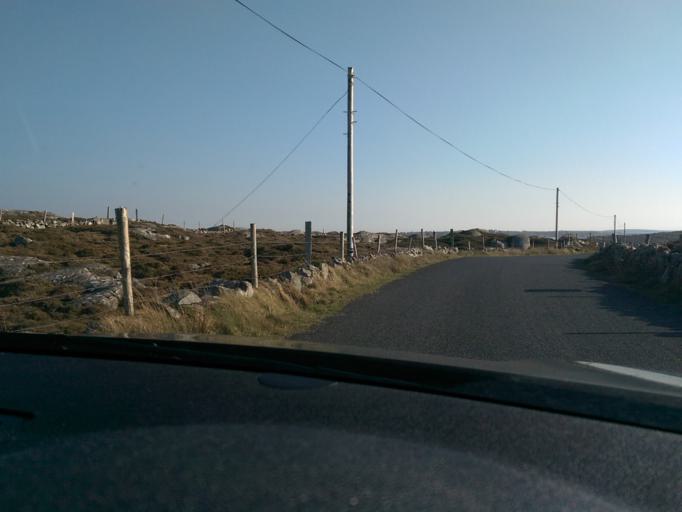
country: IE
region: Connaught
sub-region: County Galway
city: Clifden
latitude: 53.3635
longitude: -9.8793
